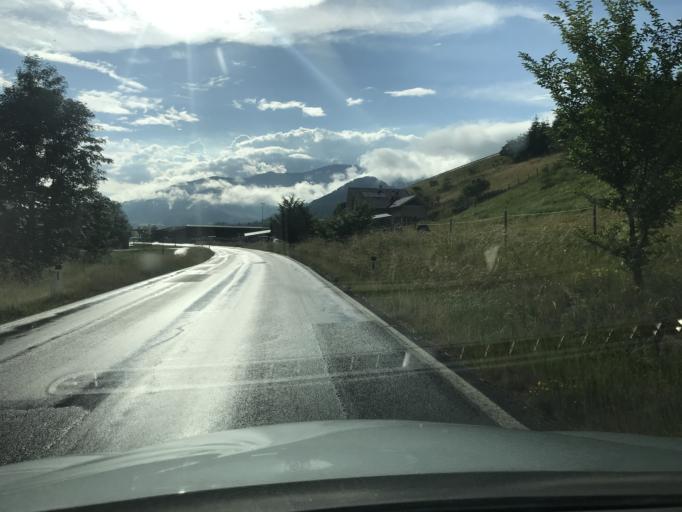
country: AT
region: Styria
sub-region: Politischer Bezirk Murau
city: Sankt Peter am Kammersberg
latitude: 47.1864
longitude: 14.1852
